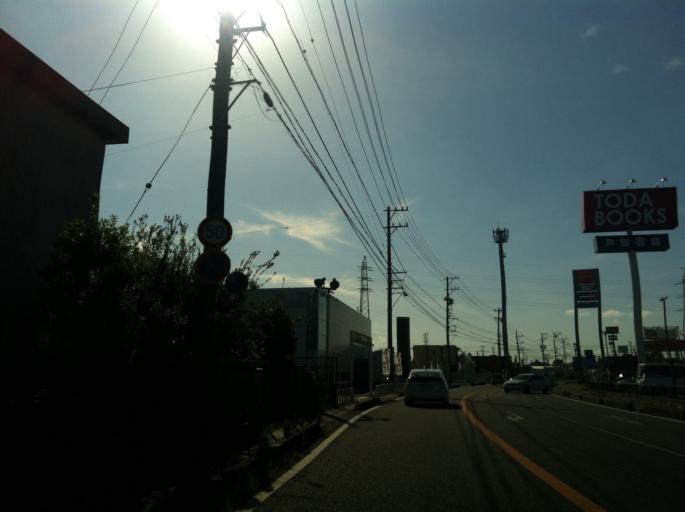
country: JP
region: Shizuoka
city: Fujieda
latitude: 34.8738
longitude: 138.2689
